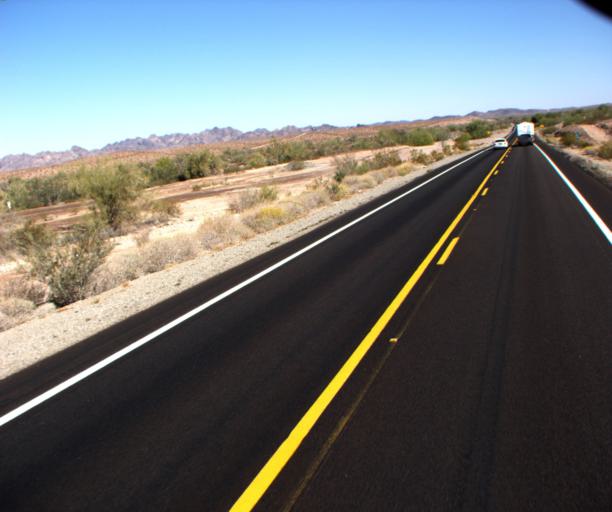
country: US
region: Arizona
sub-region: La Paz County
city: Quartzsite
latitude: 33.1613
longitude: -114.2795
